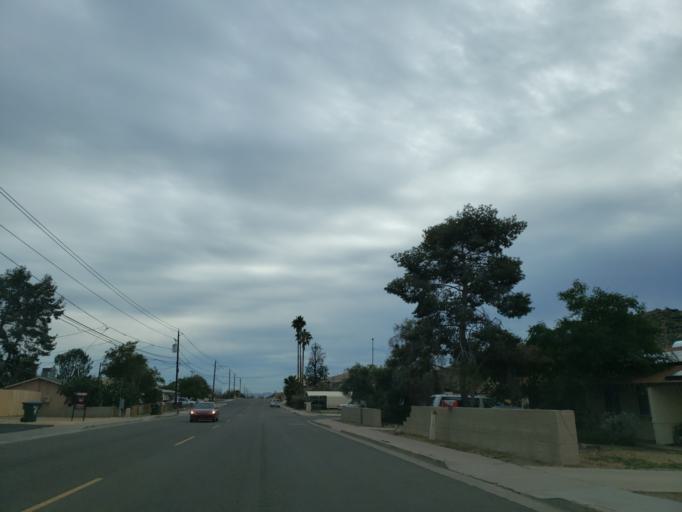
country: US
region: Arizona
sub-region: Maricopa County
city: Glendale
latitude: 33.5799
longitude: -112.0913
